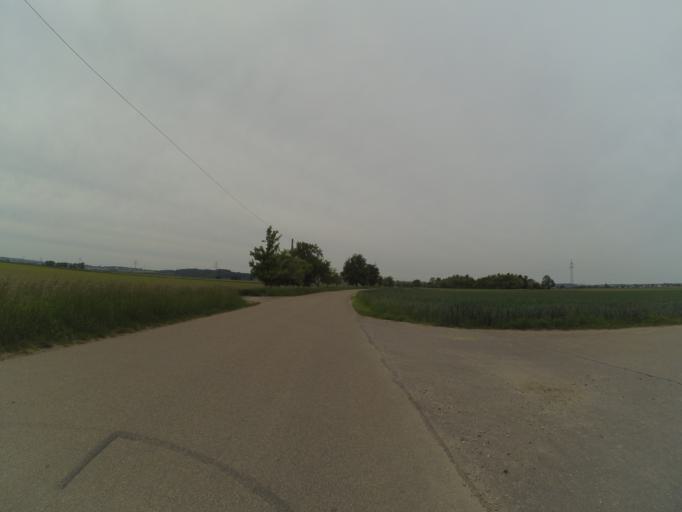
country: DE
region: Baden-Wuerttemberg
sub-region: Regierungsbezirk Stuttgart
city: Sontheim an der Brenz
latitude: 48.5312
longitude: 10.2857
